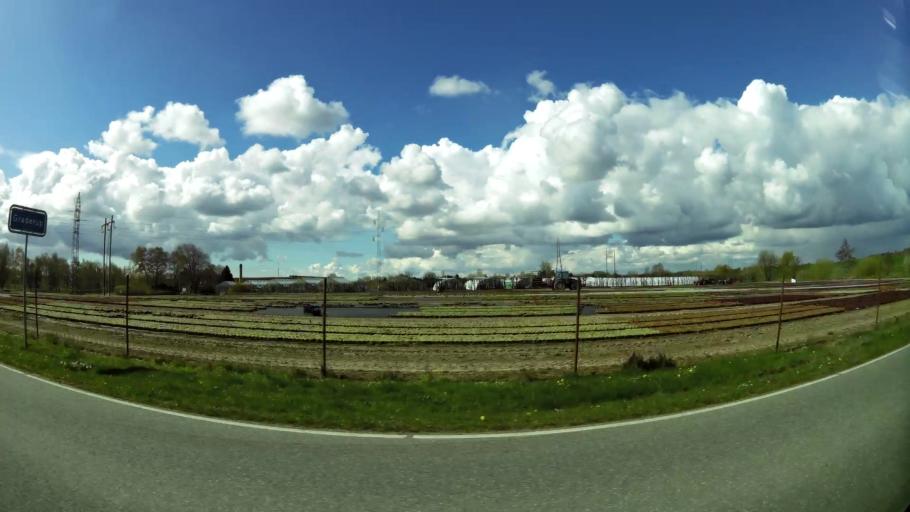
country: DK
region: South Denmark
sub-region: Middelfart Kommune
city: Brenderup
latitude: 55.4721
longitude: 10.0014
